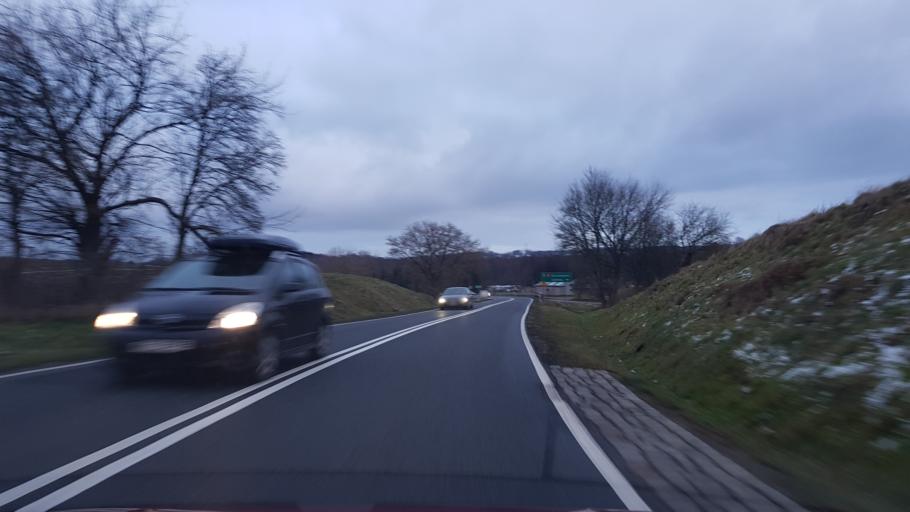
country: PL
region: Pomeranian Voivodeship
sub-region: Powiat bytowski
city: Tuchomie
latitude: 54.1020
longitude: 17.3216
